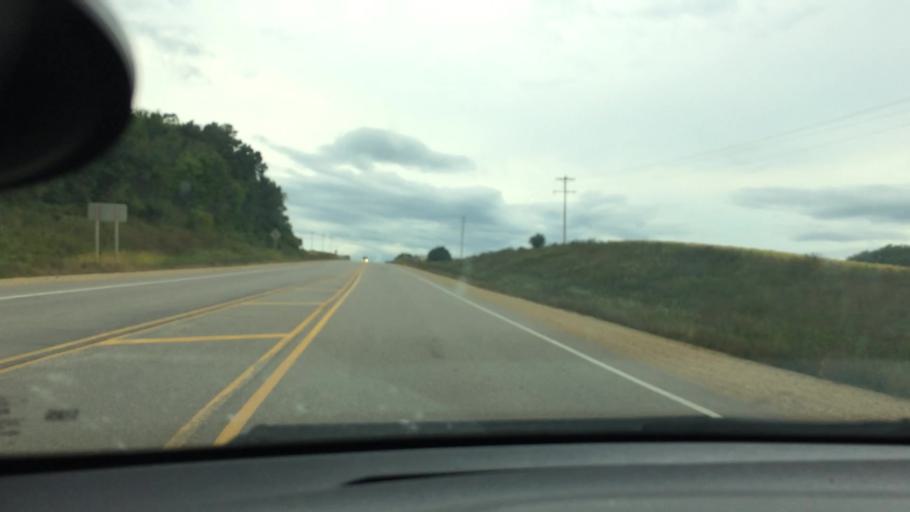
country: US
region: Wisconsin
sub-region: Trempealeau County
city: Osseo
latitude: 44.5895
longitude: -91.1785
